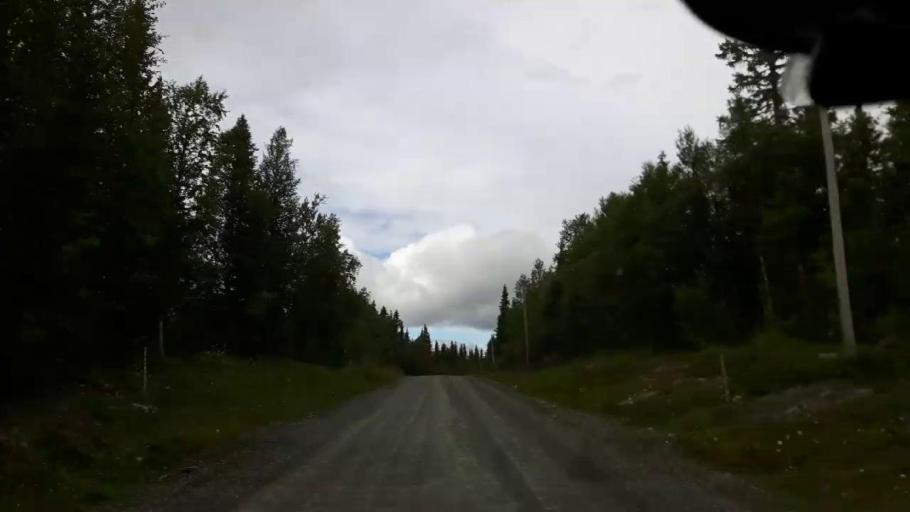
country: SE
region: Jaemtland
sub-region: Krokoms Kommun
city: Valla
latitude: 63.7273
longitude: 13.8414
